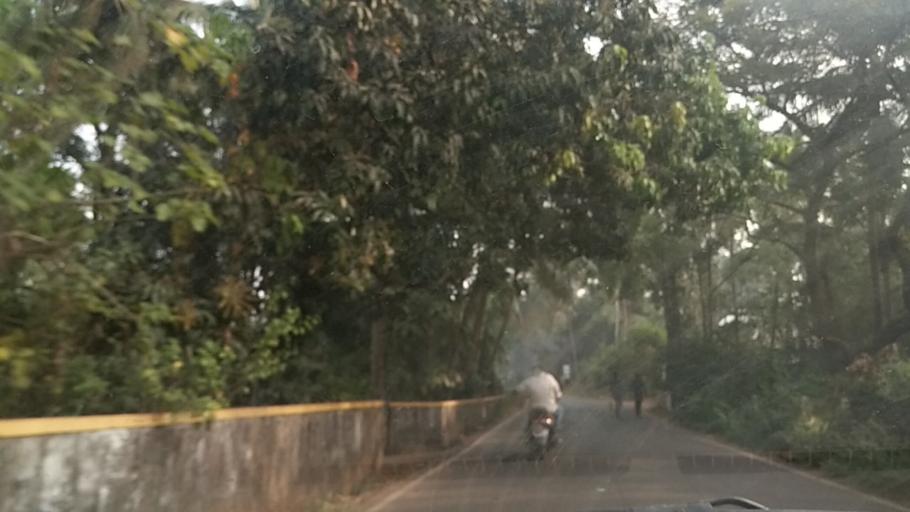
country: IN
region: Goa
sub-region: South Goa
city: Benaulim
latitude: 15.2668
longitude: 73.9460
